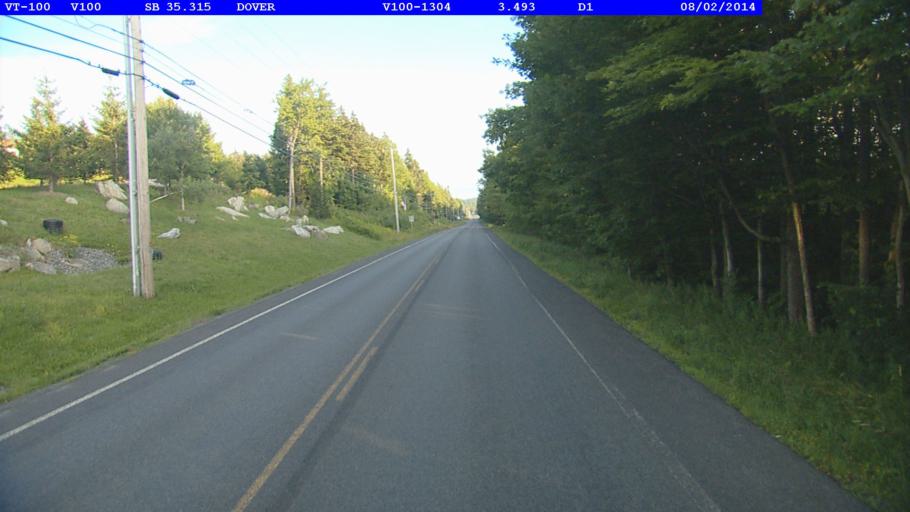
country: US
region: Vermont
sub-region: Windham County
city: Dover
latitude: 42.9617
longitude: -72.8851
